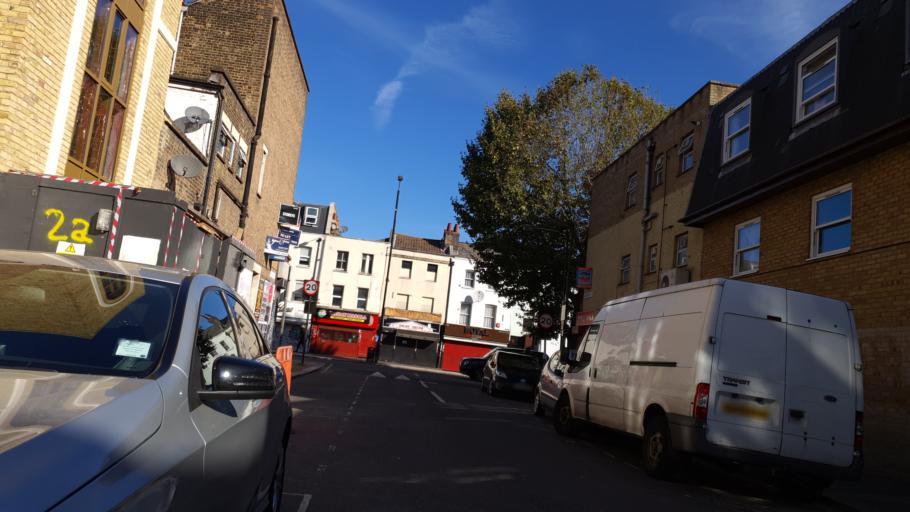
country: GB
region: England
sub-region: Greater London
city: Bethnal Green
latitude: 51.5259
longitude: -0.0660
